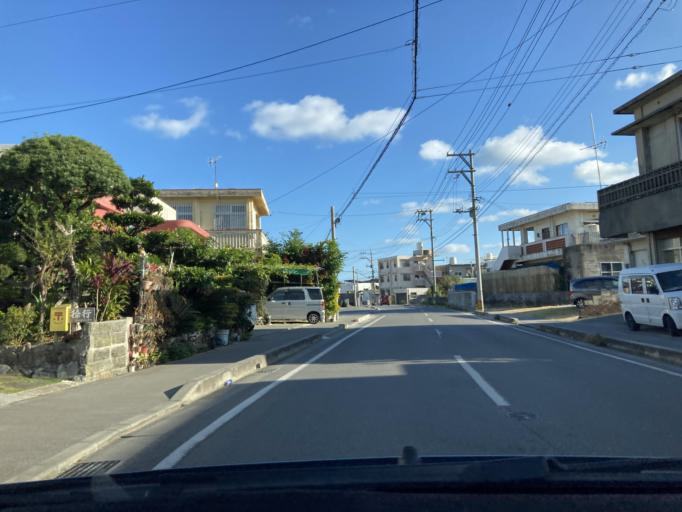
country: JP
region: Okinawa
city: Katsuren-haebaru
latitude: 26.3266
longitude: 127.9027
